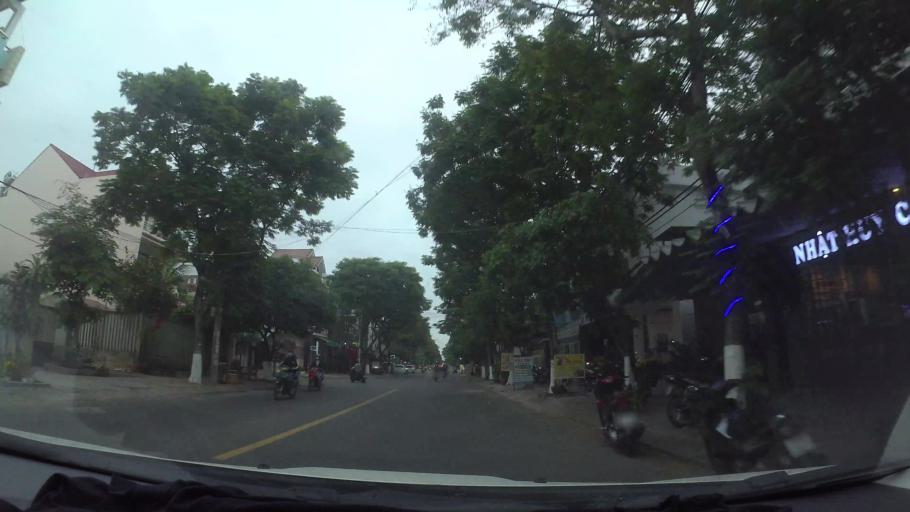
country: VN
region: Da Nang
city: Lien Chieu
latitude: 16.0777
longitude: 108.1604
